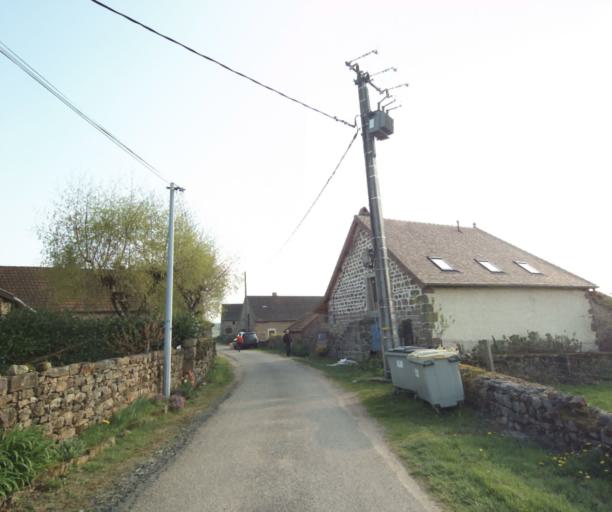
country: FR
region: Bourgogne
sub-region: Departement de Saone-et-Loire
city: Matour
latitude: 46.4263
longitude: 4.4821
